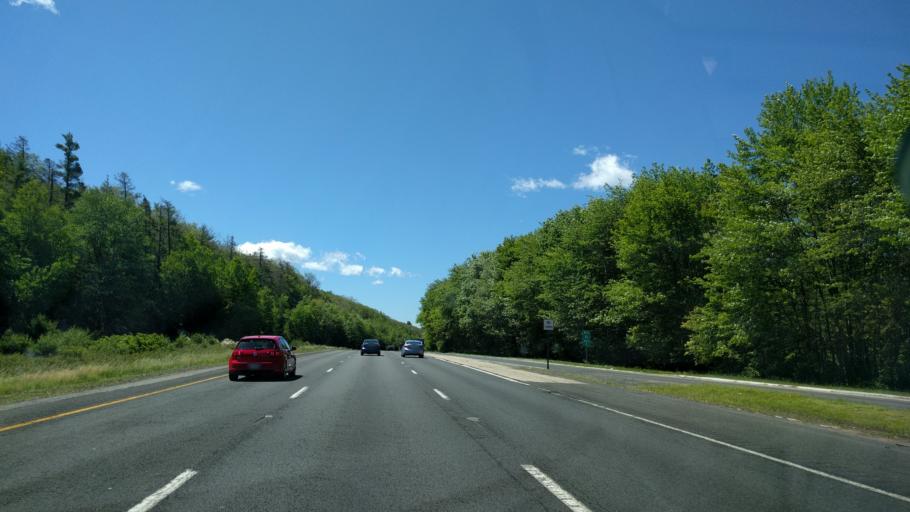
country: US
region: Massachusetts
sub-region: Worcester County
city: Sturbridge
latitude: 42.0815
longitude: -72.0982
